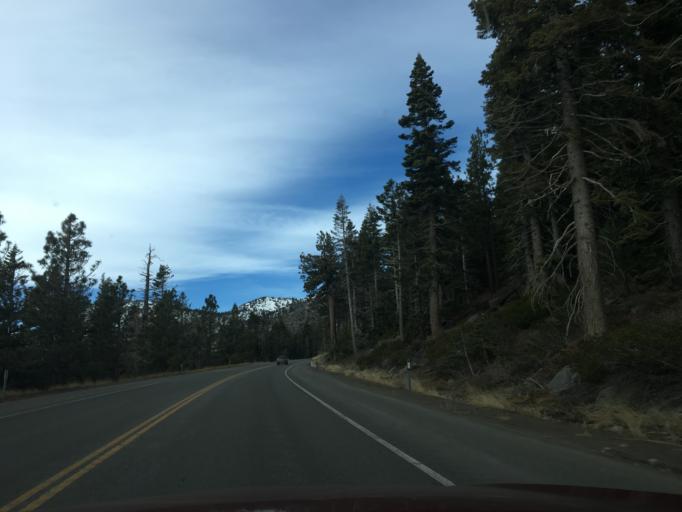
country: US
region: Nevada
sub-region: Washoe County
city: Incline Village
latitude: 39.2695
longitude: -119.9317
